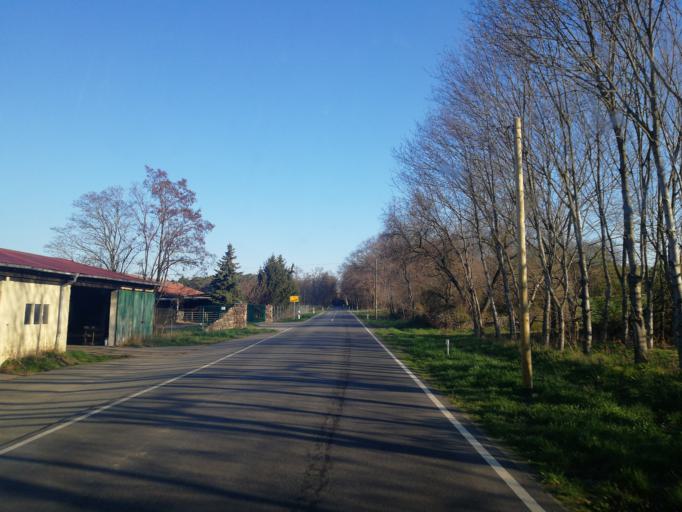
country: DE
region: Brandenburg
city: Drahnsdorf
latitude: 51.8962
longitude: 13.6076
